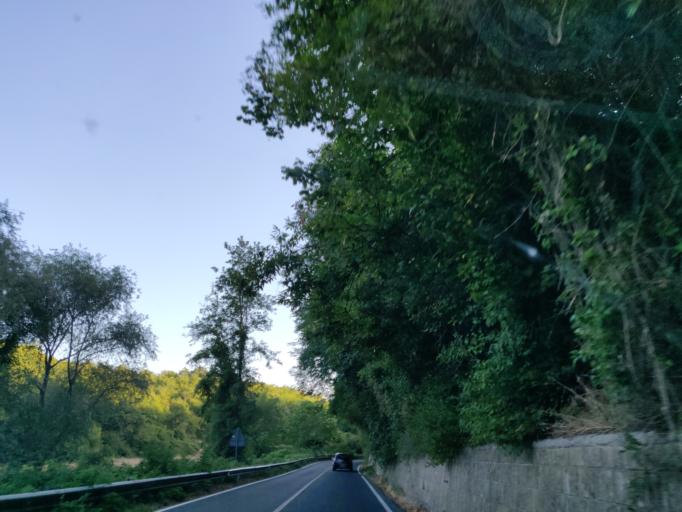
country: IT
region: Latium
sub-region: Provincia di Viterbo
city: Gradoli
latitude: 42.6567
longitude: 11.8476
